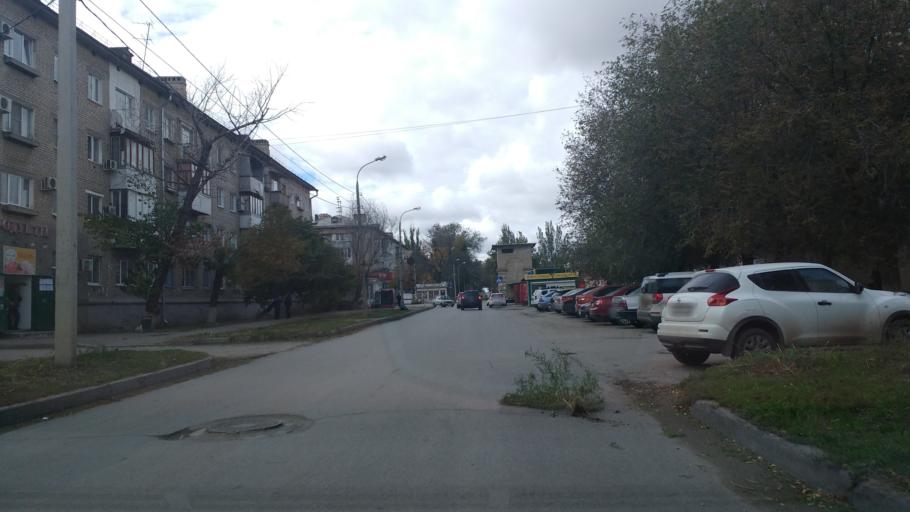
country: RU
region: Volgograd
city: Vodstroy
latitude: 48.7744
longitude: 44.5462
